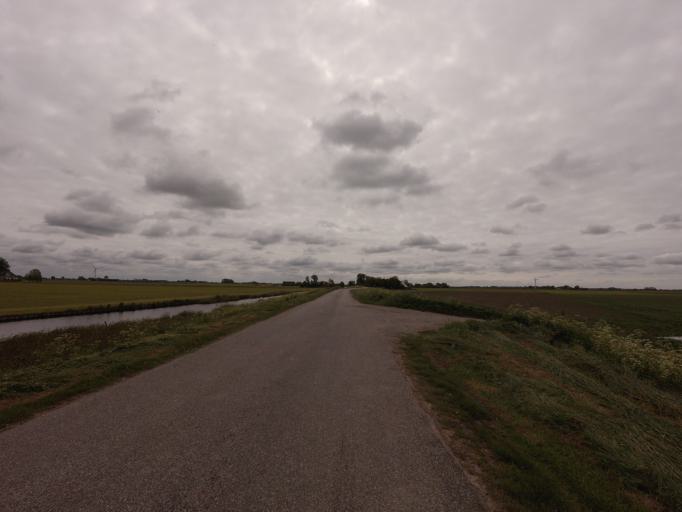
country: NL
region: Friesland
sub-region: Sudwest Fryslan
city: Workum
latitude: 52.9597
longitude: 5.4441
